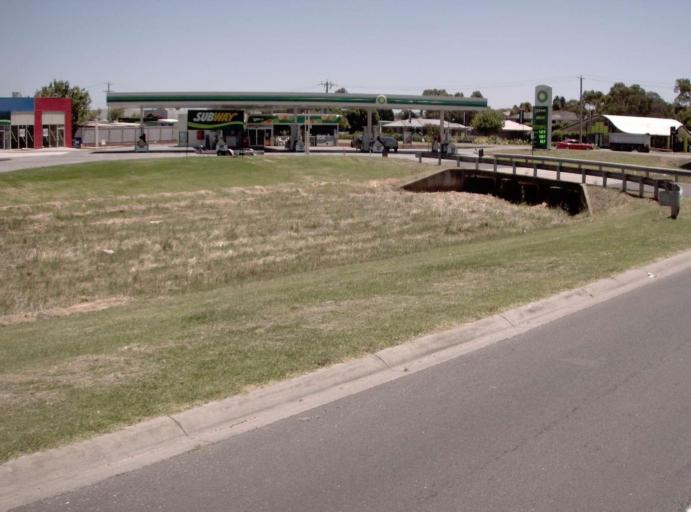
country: AU
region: Victoria
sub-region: Casey
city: Narre Warren
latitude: -38.0187
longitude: 145.2959
